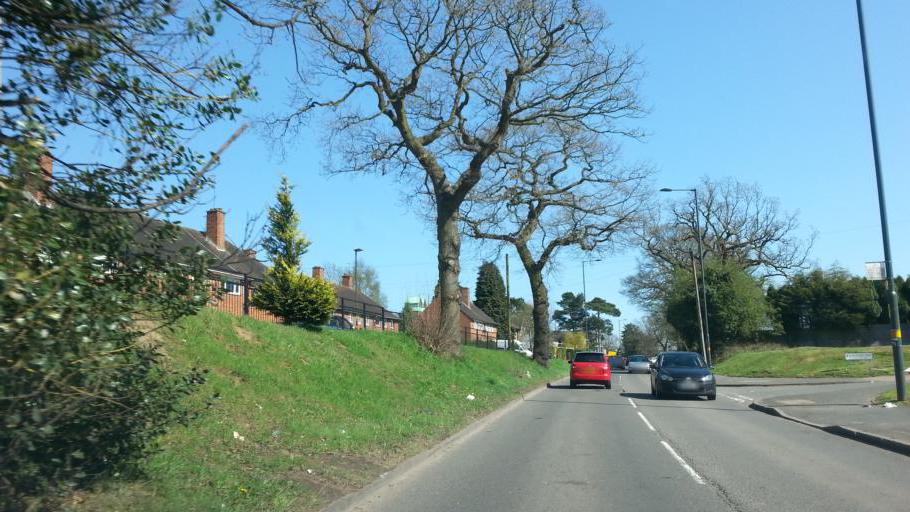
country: GB
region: England
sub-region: City and Borough of Birmingham
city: Bartley Green
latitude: 52.3952
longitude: -1.9776
